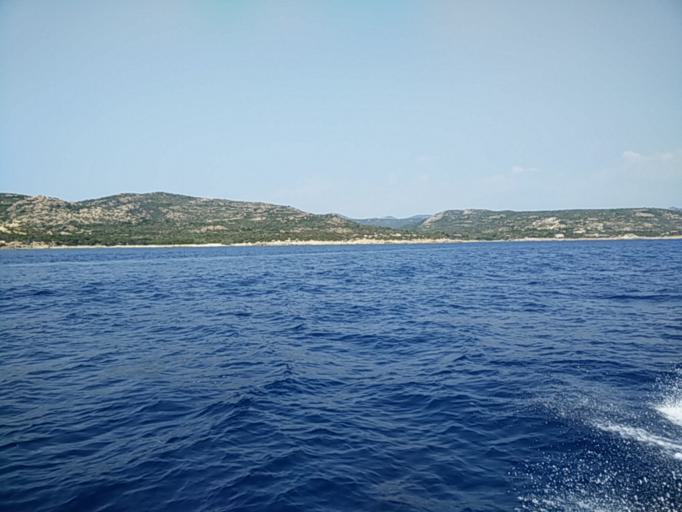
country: FR
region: Corsica
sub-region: Departement de la Corse-du-Sud
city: Propriano
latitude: 41.5414
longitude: 8.8238
